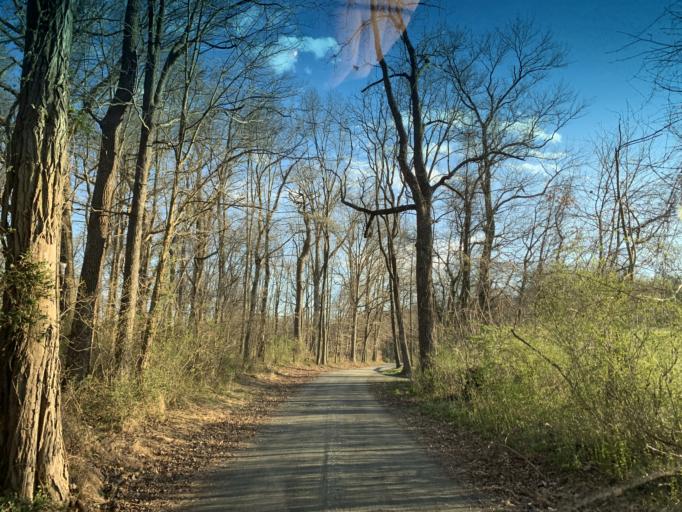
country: US
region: Maryland
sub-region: Harford County
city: Aberdeen
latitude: 39.6117
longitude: -76.2200
